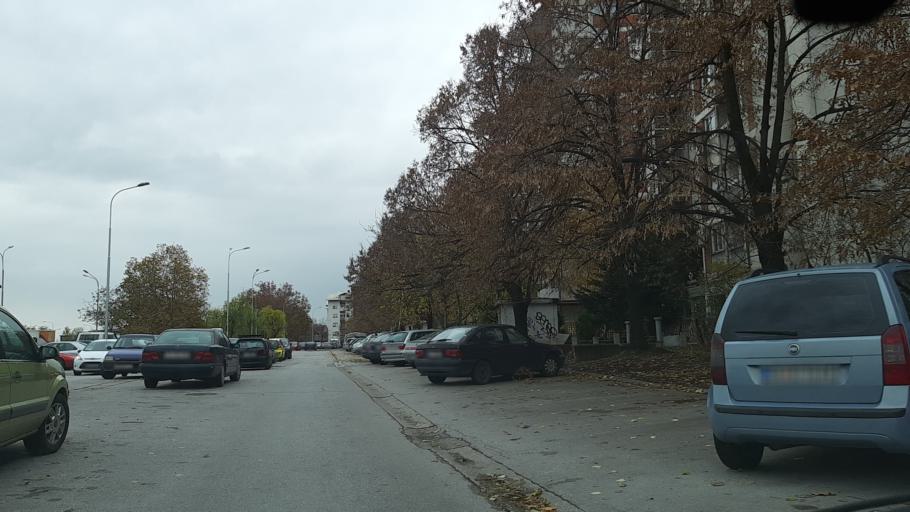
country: MK
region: Kisela Voda
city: Usje
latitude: 41.9916
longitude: 21.4669
